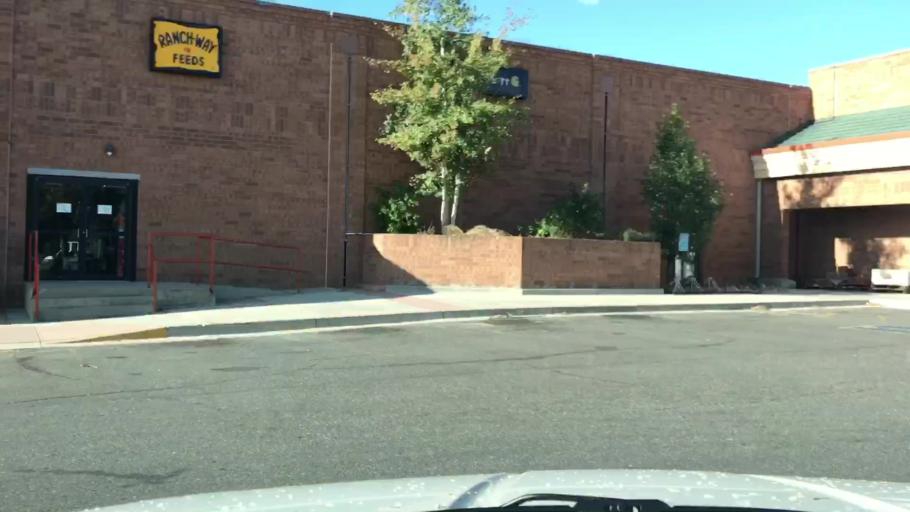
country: US
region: Colorado
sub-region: Boulder County
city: Lafayette
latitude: 39.9860
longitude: -105.0952
